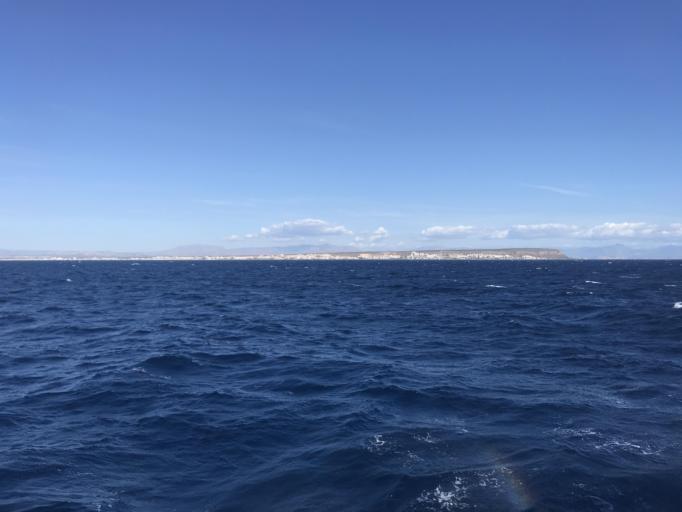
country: ES
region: Valencia
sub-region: Provincia de Alicante
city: Santa Pola
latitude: 38.1383
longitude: -0.5275
